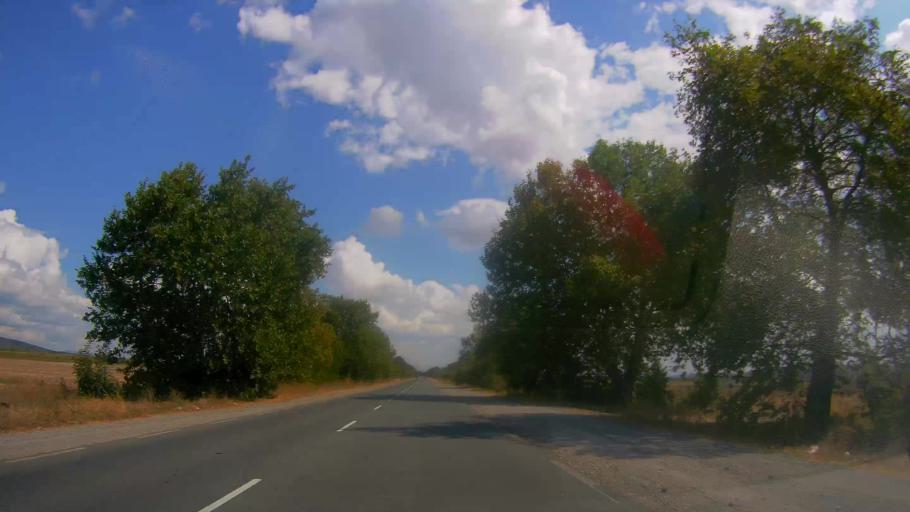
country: BG
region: Sliven
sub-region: Obshtina Sliven
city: Kermen
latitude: 42.6346
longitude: 26.1613
